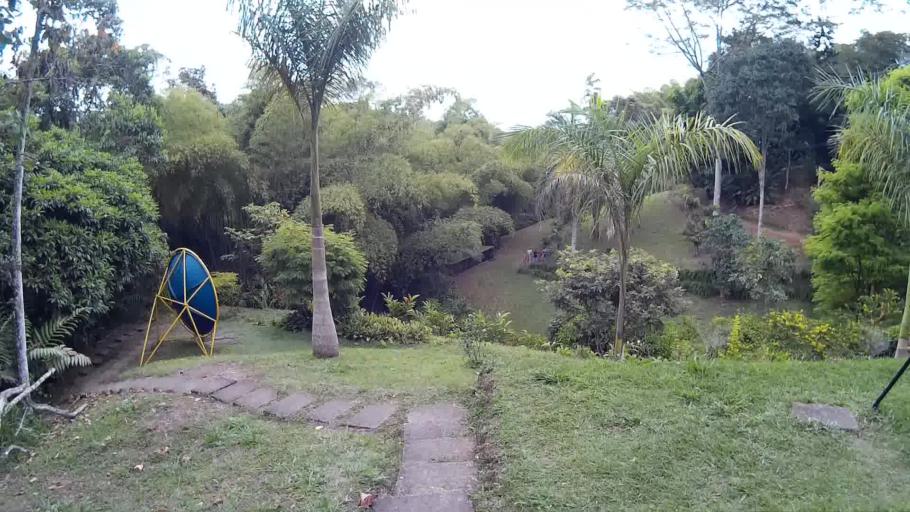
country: CO
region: Risaralda
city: Marsella
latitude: 4.9334
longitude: -75.7368
